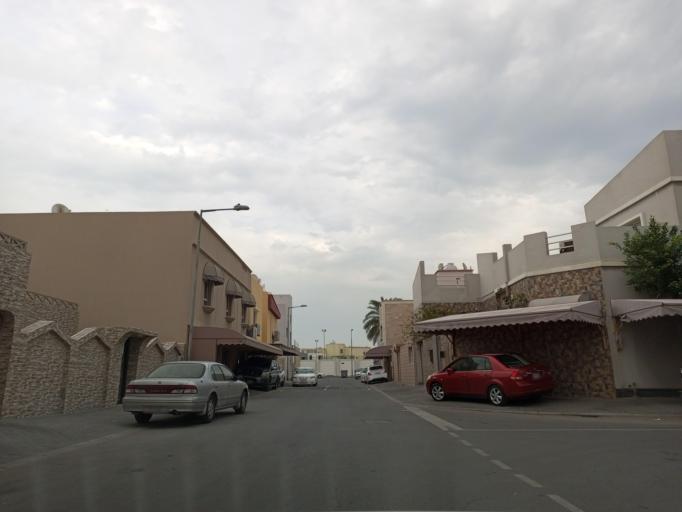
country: BH
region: Muharraq
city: Al Muharraq
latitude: 26.2568
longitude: 50.6288
